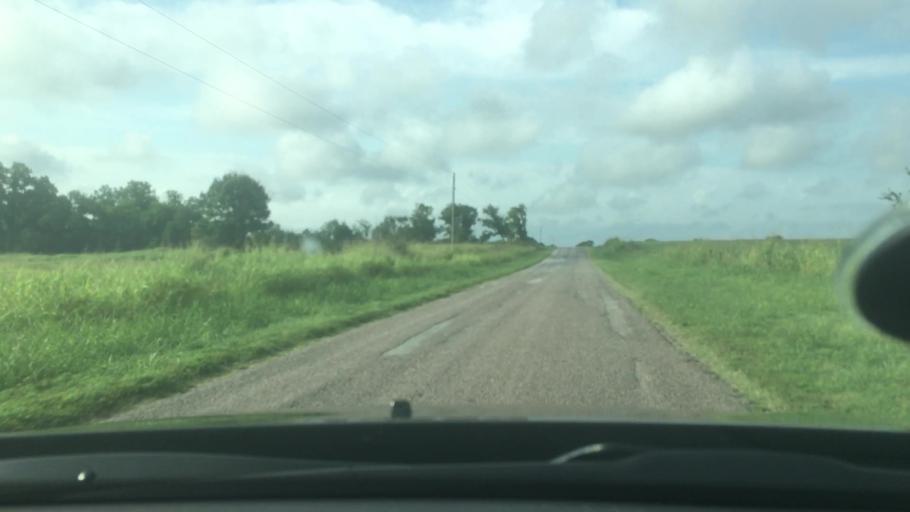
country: US
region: Oklahoma
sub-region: Pontotoc County
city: Ada
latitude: 34.6854
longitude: -96.5298
